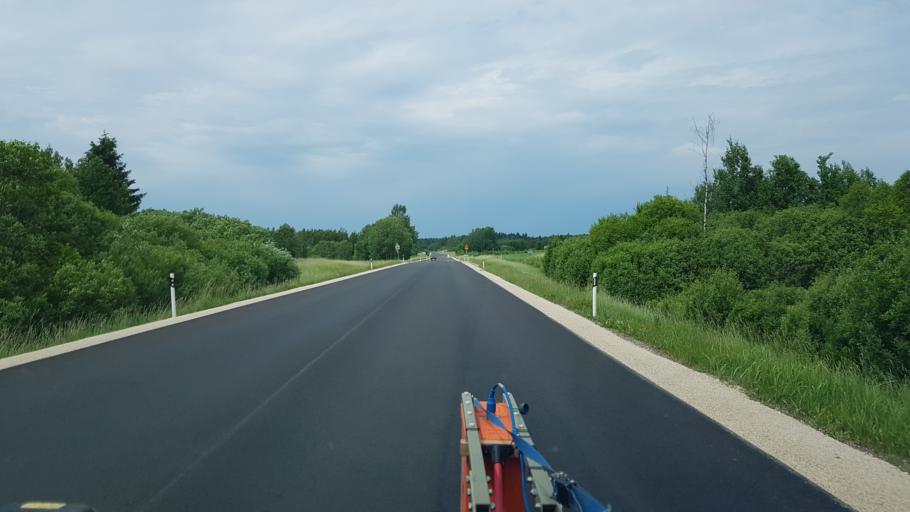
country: EE
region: Vorumaa
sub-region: Voru linn
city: Voru
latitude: 57.7575
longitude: 27.2143
